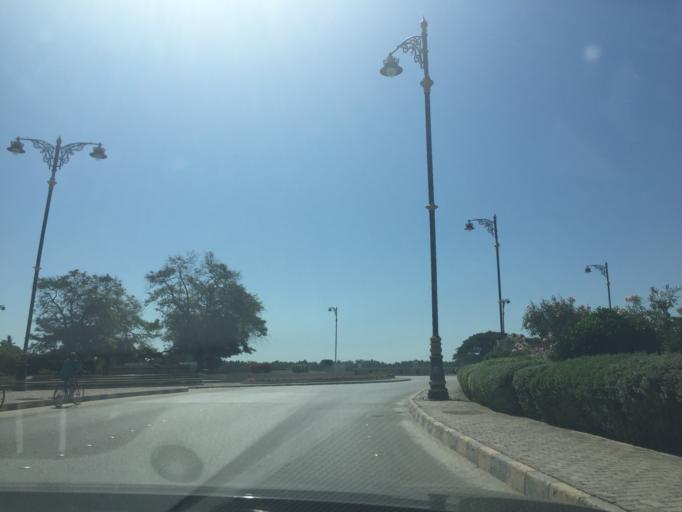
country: OM
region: Zufar
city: Salalah
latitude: 17.0270
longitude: 54.1434
